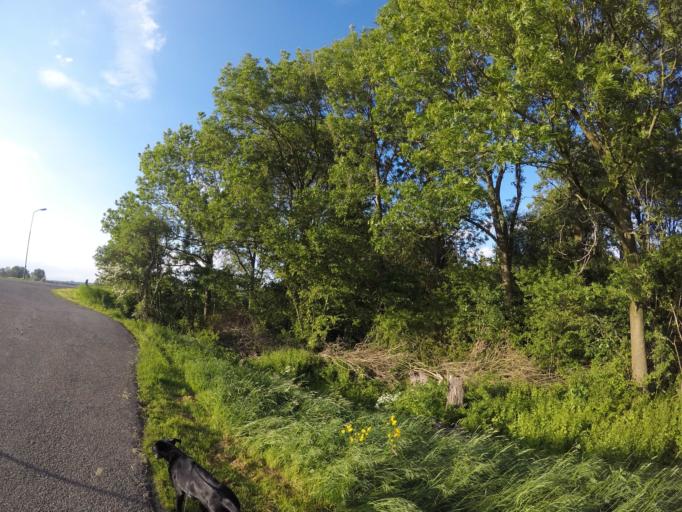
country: NL
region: Gelderland
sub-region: Gemeente Westervoort
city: Westervoort
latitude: 51.9545
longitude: 5.9640
